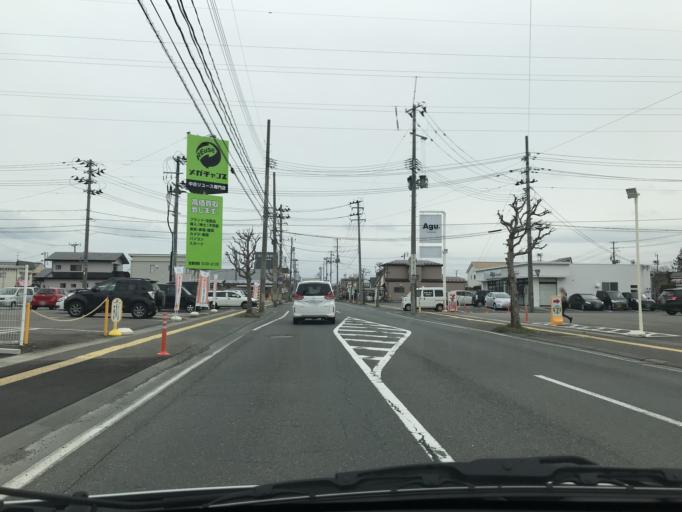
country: JP
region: Iwate
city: Hanamaki
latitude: 39.3929
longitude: 141.1077
